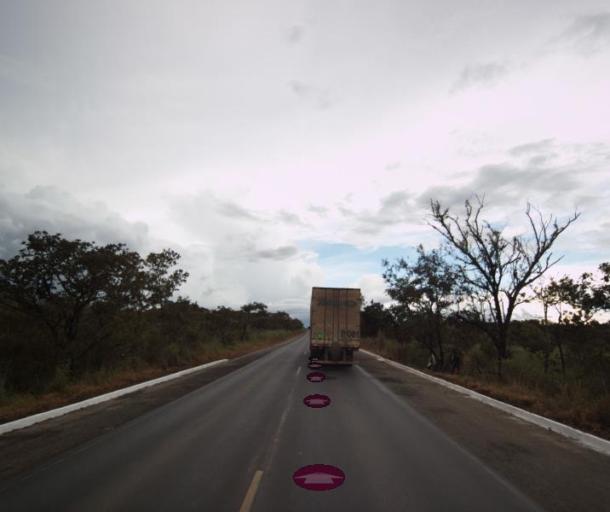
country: BR
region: Goias
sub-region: Itapaci
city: Itapaci
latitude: -14.9368
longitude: -49.3693
